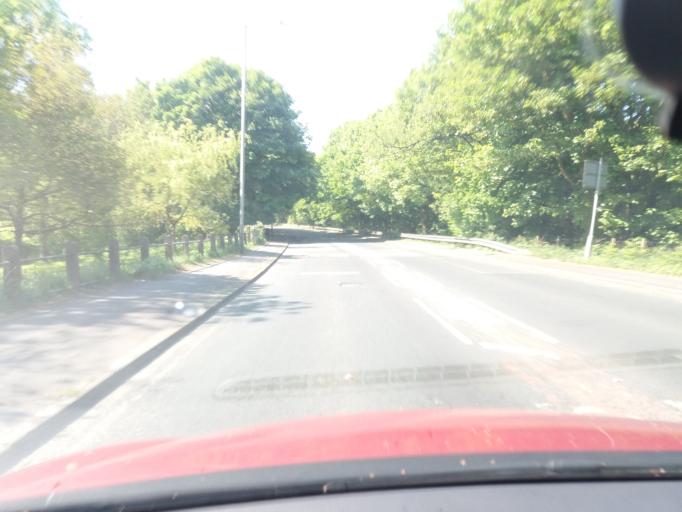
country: GB
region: England
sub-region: Lancashire
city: Coppull
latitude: 53.6351
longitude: -2.6535
